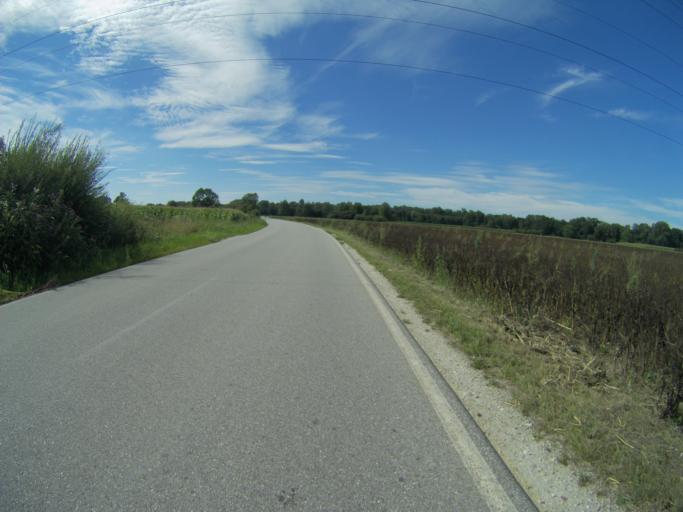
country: DE
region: Bavaria
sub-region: Upper Bavaria
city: Marzling
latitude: 48.3956
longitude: 11.7967
